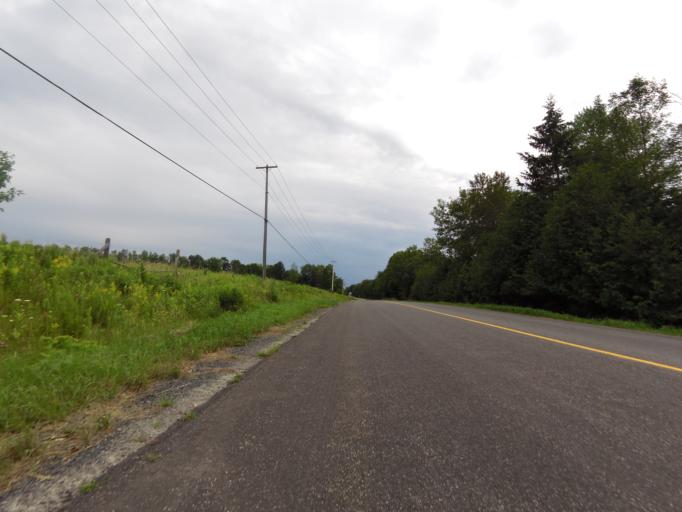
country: CA
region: Ontario
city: Perth
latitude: 45.0898
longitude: -76.3997
